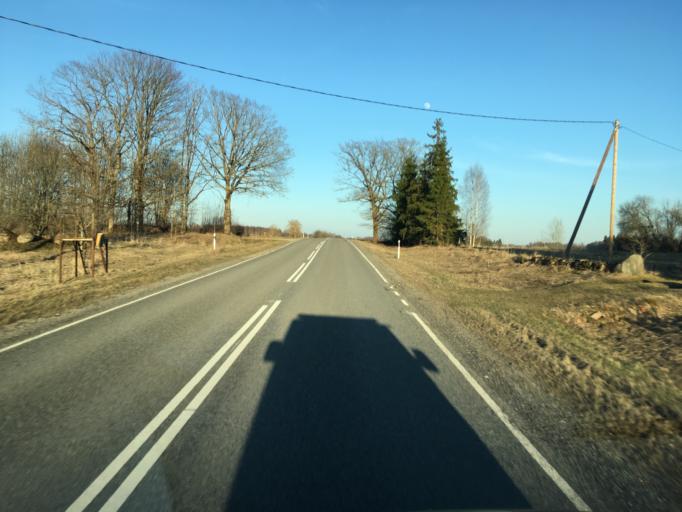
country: EE
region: Raplamaa
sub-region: Rapla vald
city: Rapla
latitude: 59.0791
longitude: 24.8421
